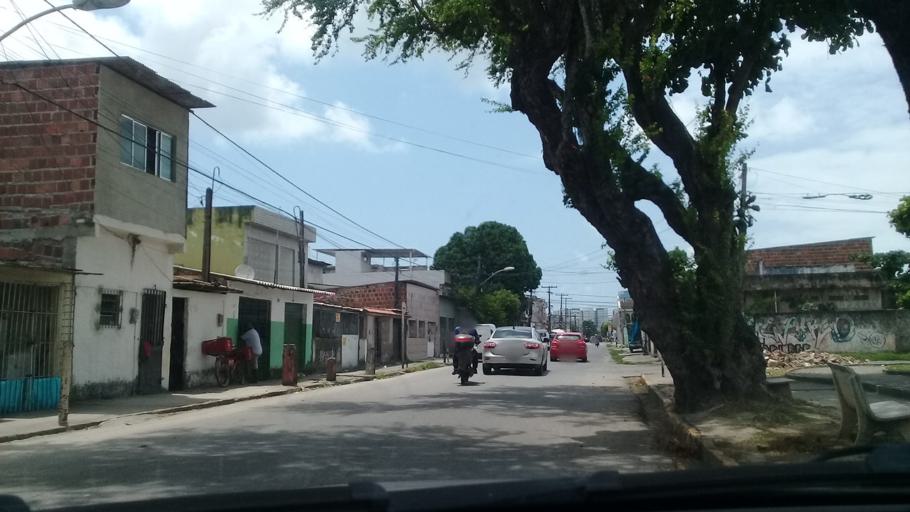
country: BR
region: Pernambuco
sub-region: Recife
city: Recife
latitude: -8.1053
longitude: -34.9196
